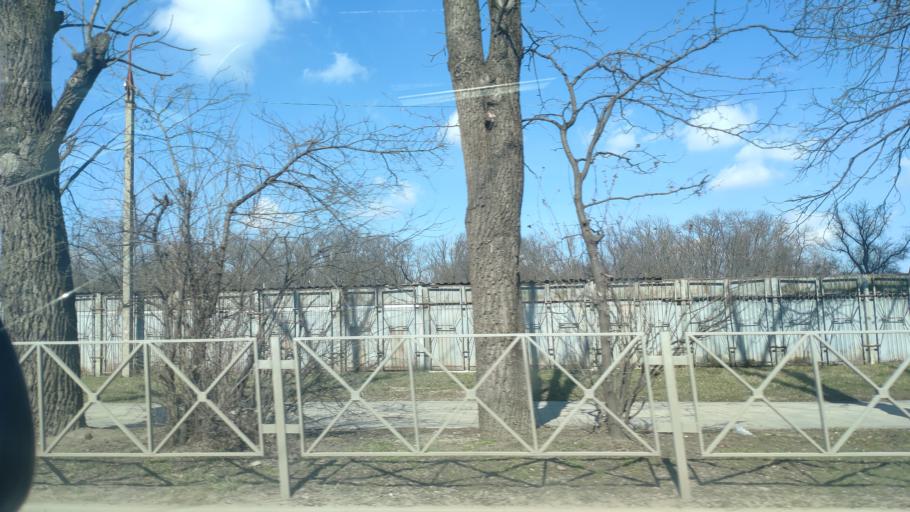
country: RU
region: Krasnodarskiy
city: Krasnodar
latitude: 45.0548
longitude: 38.9976
